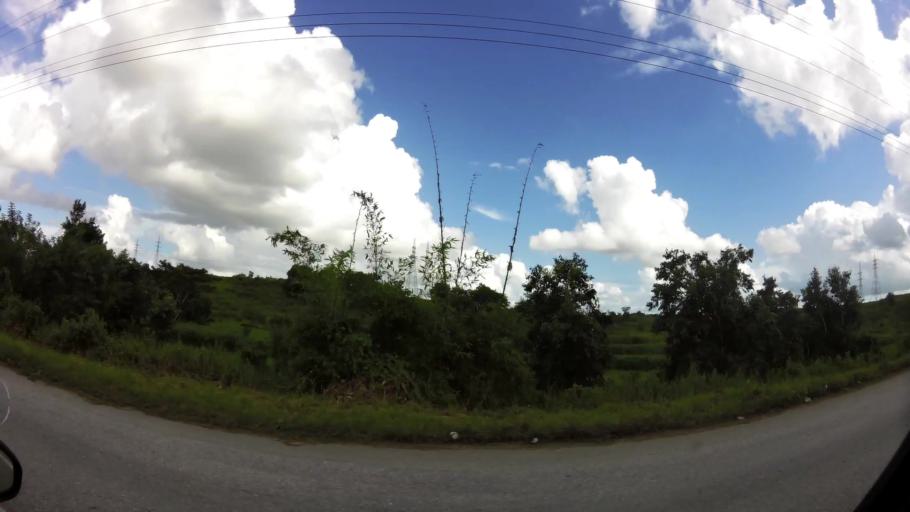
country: TT
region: Penal/Debe
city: Debe
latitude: 10.2283
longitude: -61.4352
